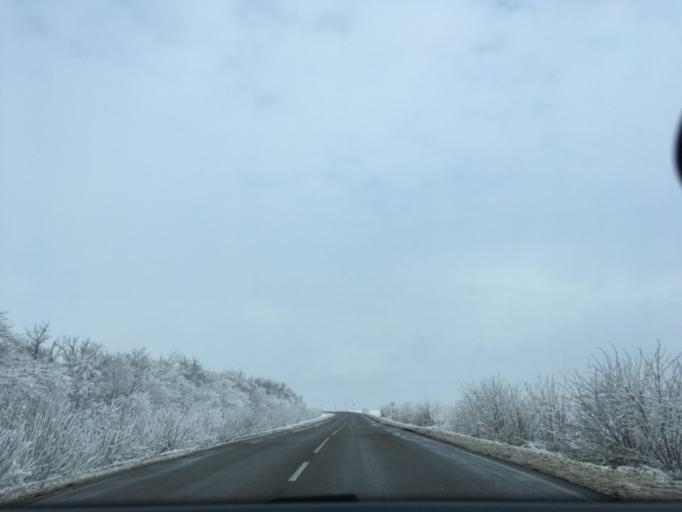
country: UA
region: Luhansk
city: Lozno-Oleksandrivka
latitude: 49.9963
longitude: 39.0372
